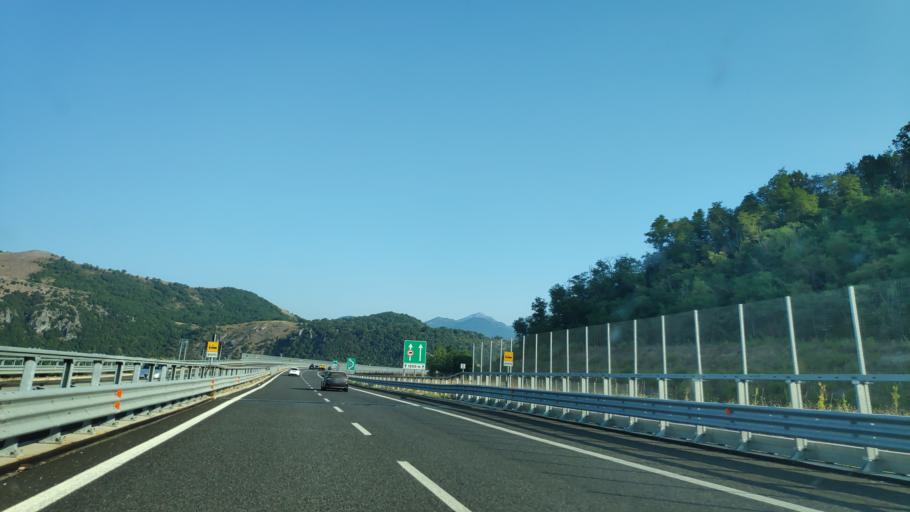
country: IT
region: Calabria
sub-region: Provincia di Cosenza
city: Laino Castello-Nuovo Centro
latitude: 39.9321
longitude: 15.9629
